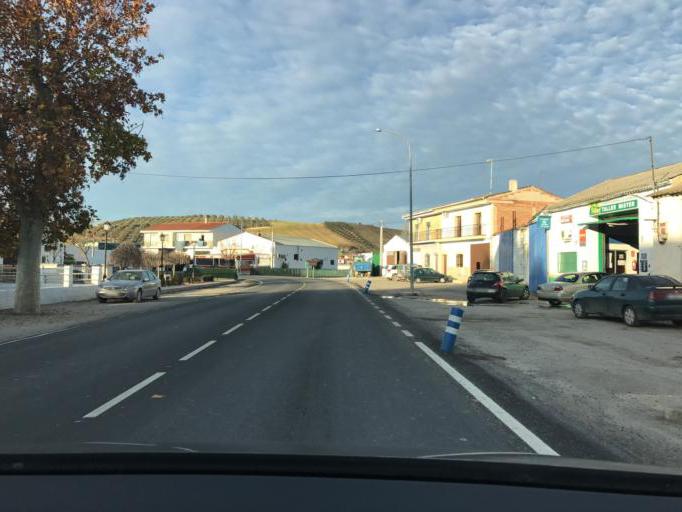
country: ES
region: Andalusia
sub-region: Provincia de Jaen
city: Guadahortuna
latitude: 37.5584
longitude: -3.3977
